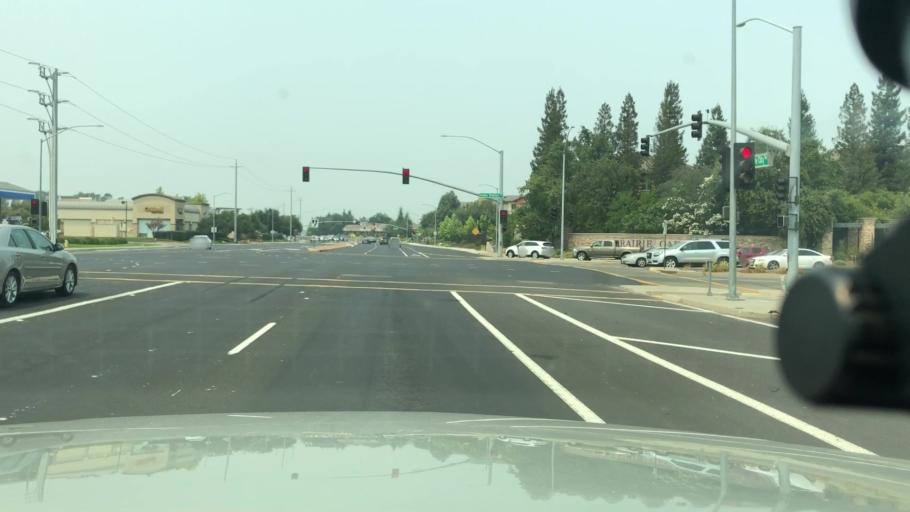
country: US
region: California
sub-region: Sacramento County
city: Folsom
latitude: 38.6493
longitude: -121.1625
